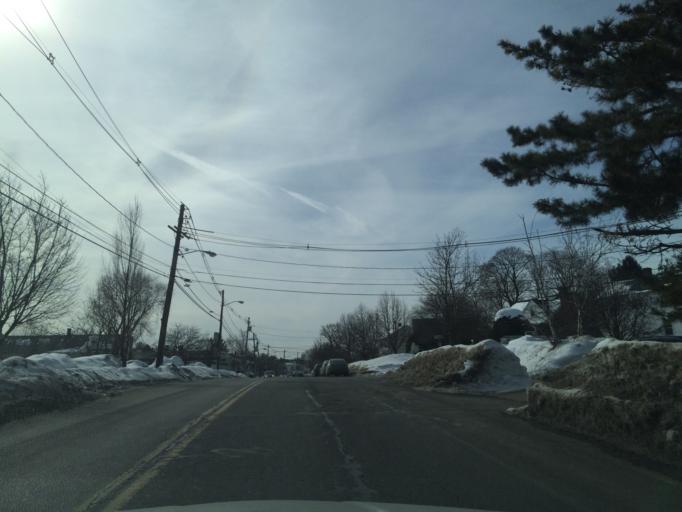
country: US
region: Massachusetts
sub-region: Middlesex County
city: Watertown
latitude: 42.3632
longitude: -71.1909
